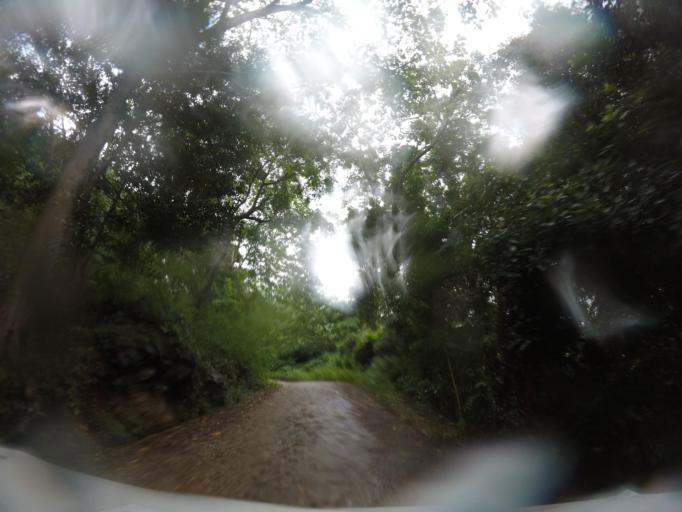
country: TL
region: Baucau
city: Venilale
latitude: -8.6286
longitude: 126.4326
